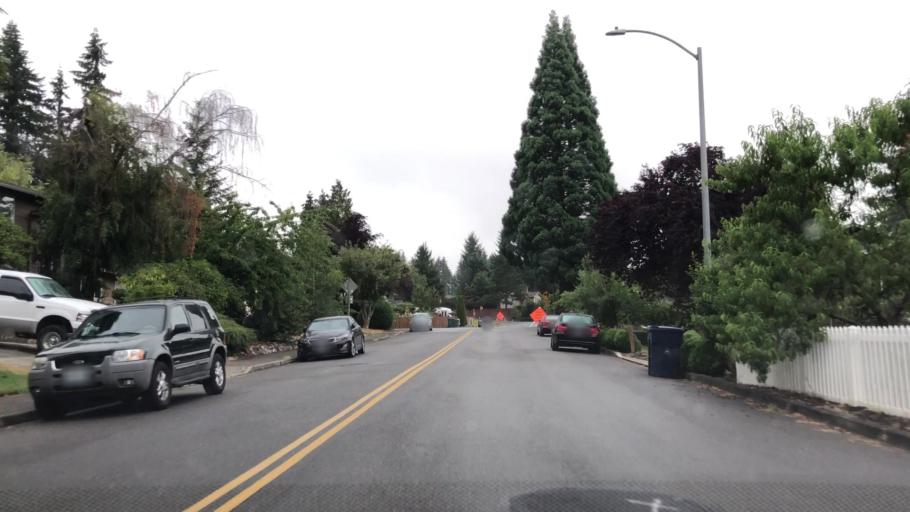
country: US
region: Washington
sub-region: Snohomish County
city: North Creek
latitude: 47.8141
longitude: -122.2146
